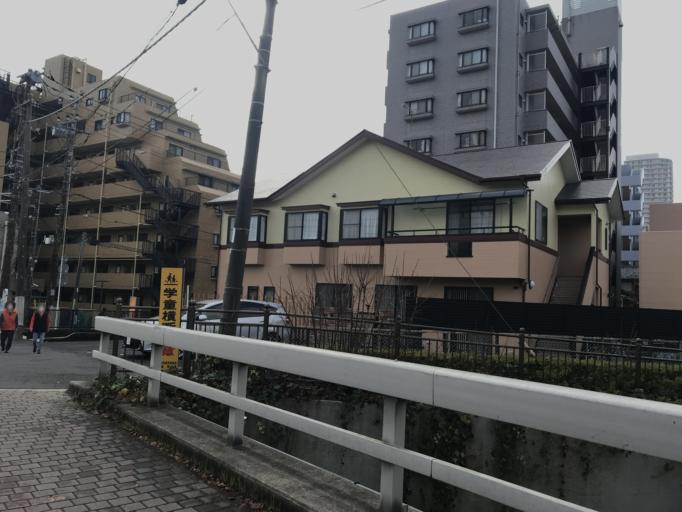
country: JP
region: Chiba
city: Funabashi
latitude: 35.7039
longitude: 139.9909
